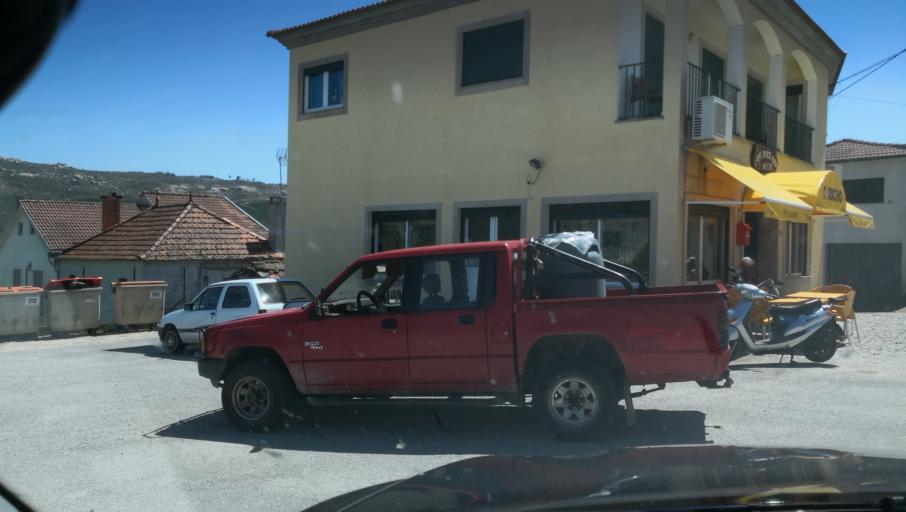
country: PT
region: Vila Real
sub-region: Sabrosa
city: Sabrosa
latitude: 41.2977
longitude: -7.6453
